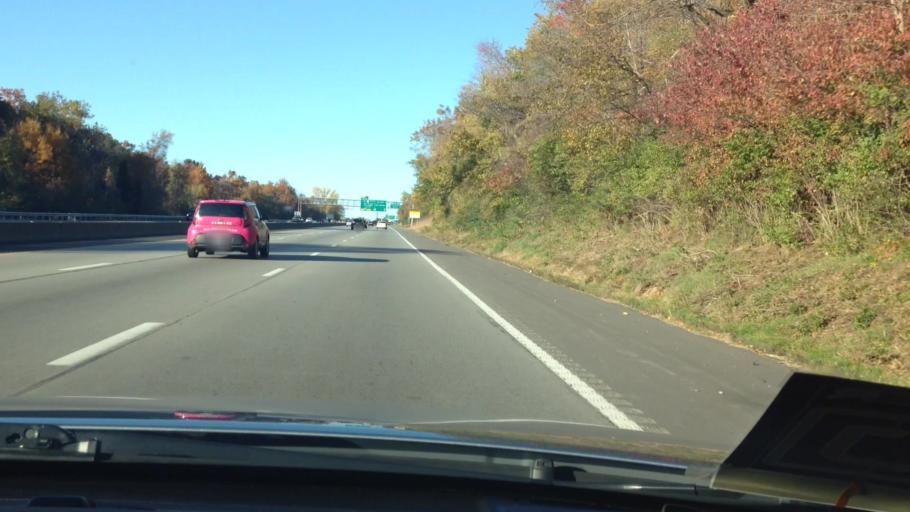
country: US
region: Missouri
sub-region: Clay County
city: North Kansas City
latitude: 39.1536
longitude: -94.5596
